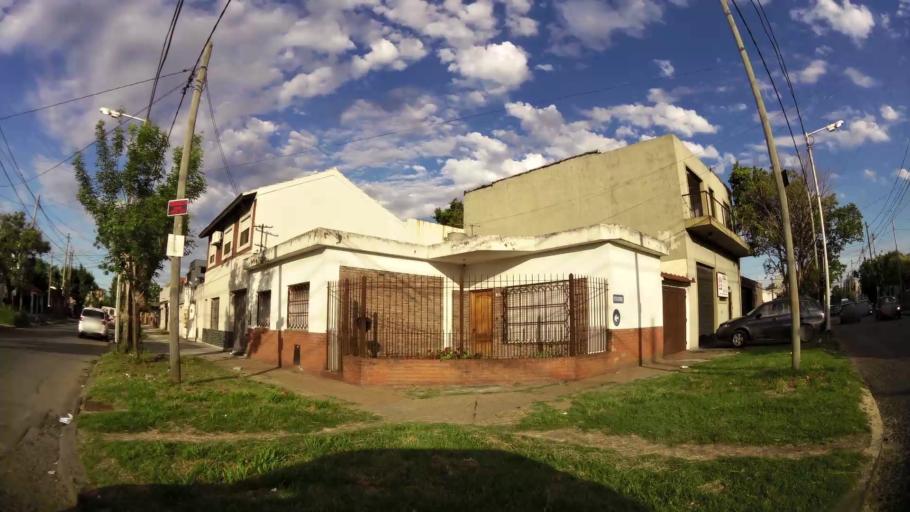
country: AR
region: Buenos Aires
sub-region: Partido de Avellaneda
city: Avellaneda
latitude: -34.6887
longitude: -58.3541
